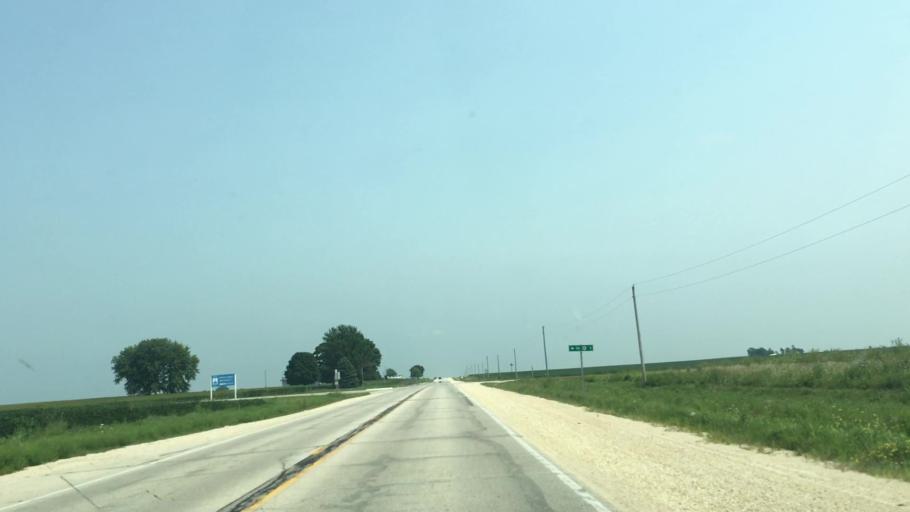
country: US
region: Iowa
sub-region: Fayette County
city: Oelwein
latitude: 42.6873
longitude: -91.8070
